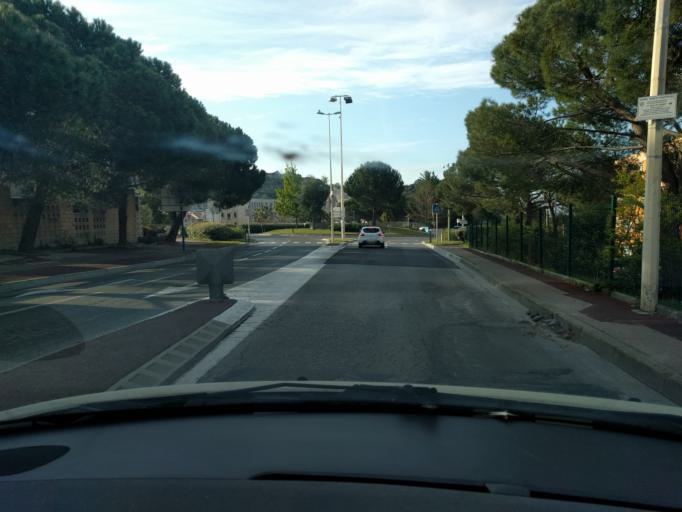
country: FR
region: Provence-Alpes-Cote d'Azur
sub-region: Departement des Alpes-Maritimes
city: Cannes
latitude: 43.5680
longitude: 6.9809
